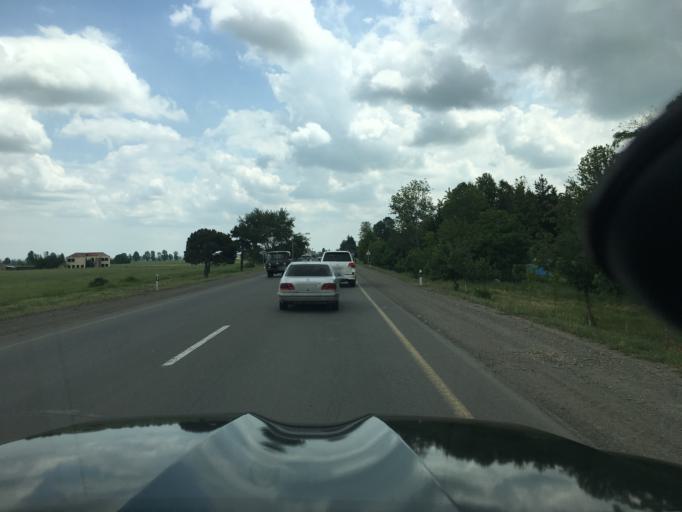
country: AZ
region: Tovuz
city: Tovuz
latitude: 40.9606
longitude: 45.7207
